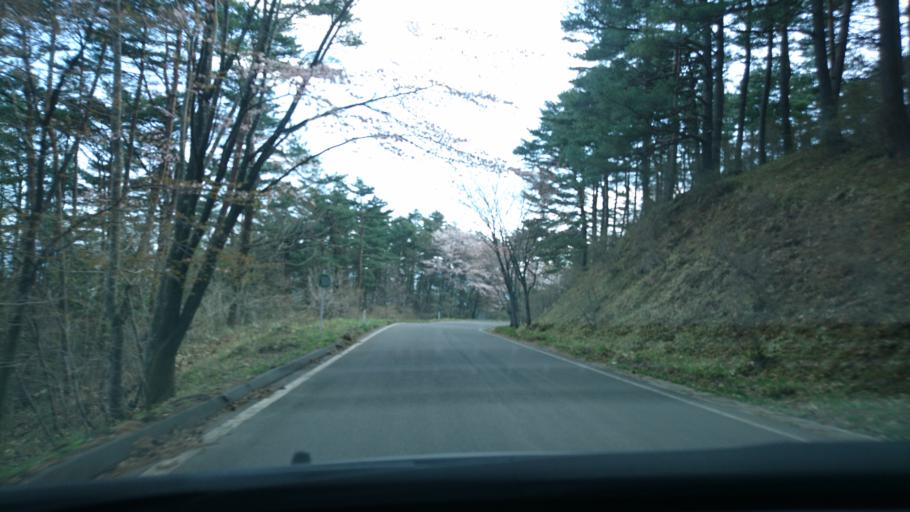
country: JP
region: Iwate
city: Ofunato
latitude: 38.9637
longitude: 141.4457
